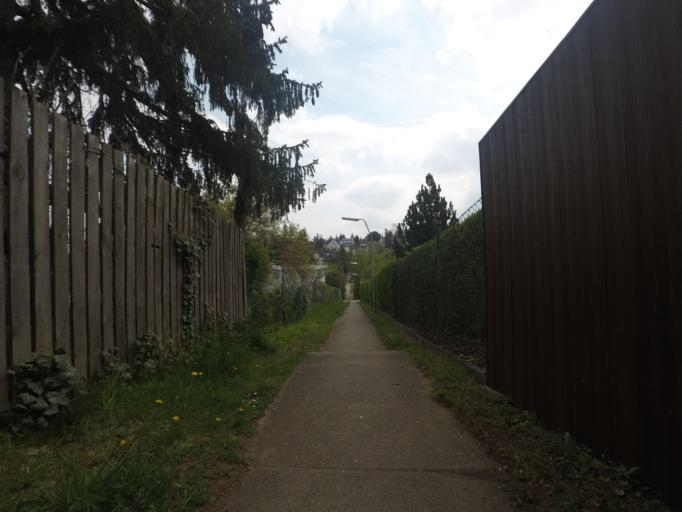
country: AT
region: Lower Austria
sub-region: Politischer Bezirk Modling
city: Perchtoldsdorf
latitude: 48.1662
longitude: 16.2662
